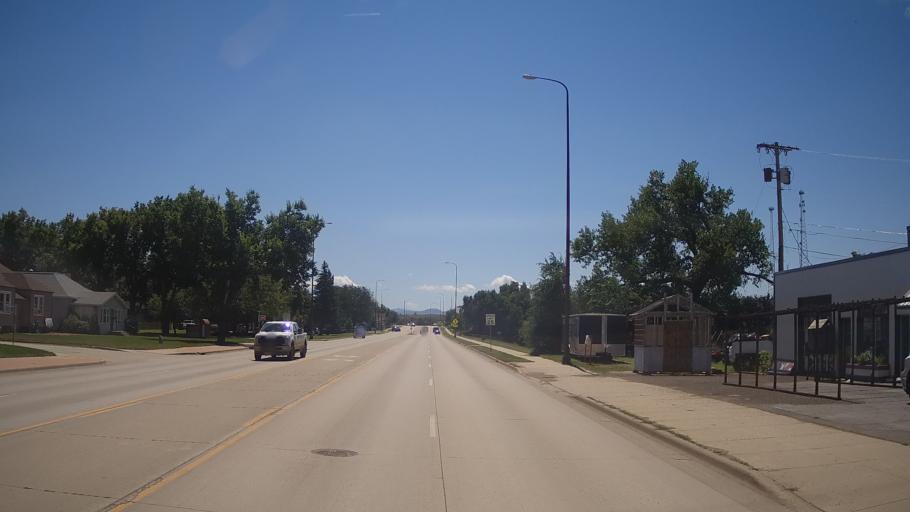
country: US
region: South Dakota
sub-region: Butte County
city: Belle Fourche
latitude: 44.6687
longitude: -103.8536
